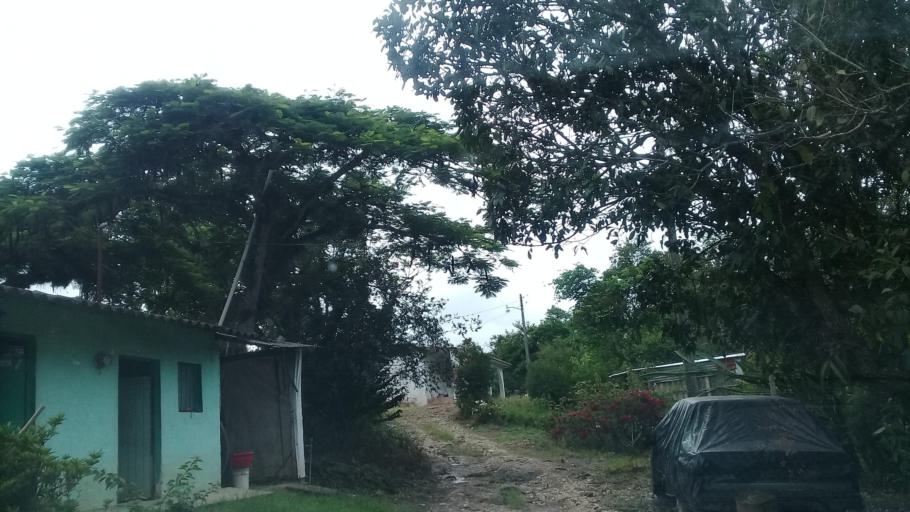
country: MX
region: Veracruz
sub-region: Emiliano Zapata
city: Jacarandas
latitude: 19.4789
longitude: -96.8498
